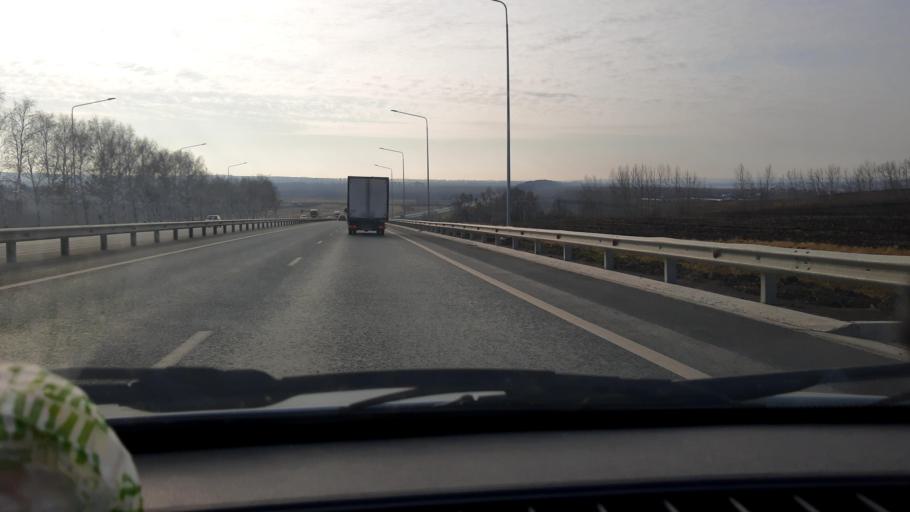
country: RU
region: Bashkortostan
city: Karmaskaly
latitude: 54.3663
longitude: 55.9152
